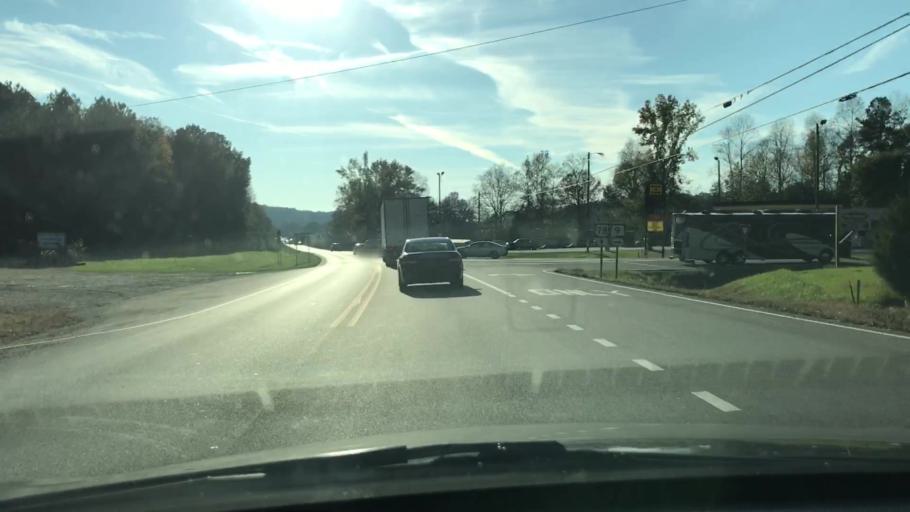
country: US
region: Alabama
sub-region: Calhoun County
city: Choccolocco
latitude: 33.6464
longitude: -85.6573
